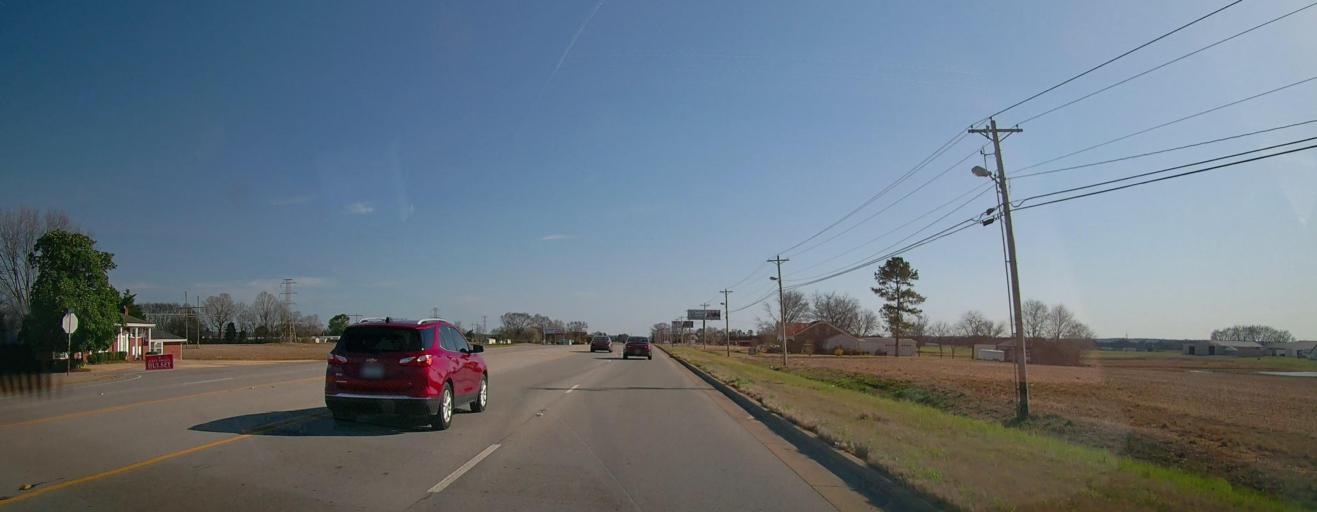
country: US
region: Alabama
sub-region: Colbert County
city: Muscle Shoals
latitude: 34.7256
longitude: -87.6351
